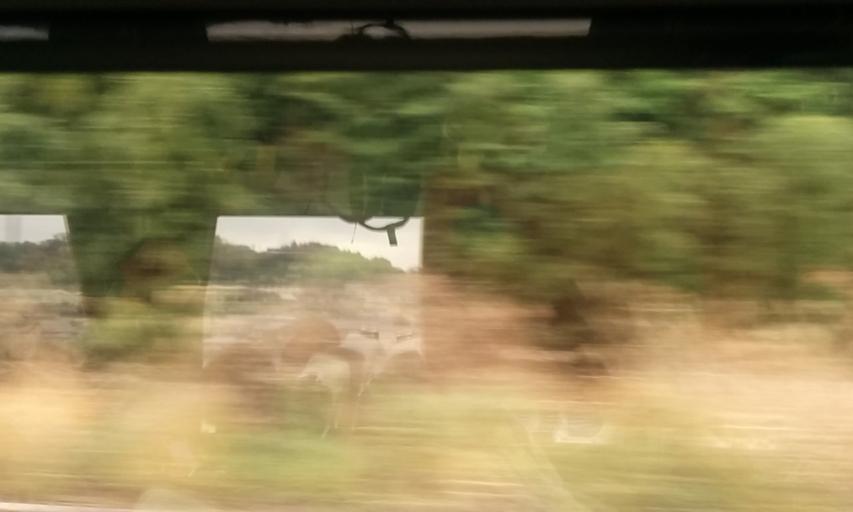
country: JP
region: Gifu
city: Nakatsugawa
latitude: 35.4939
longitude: 137.4899
